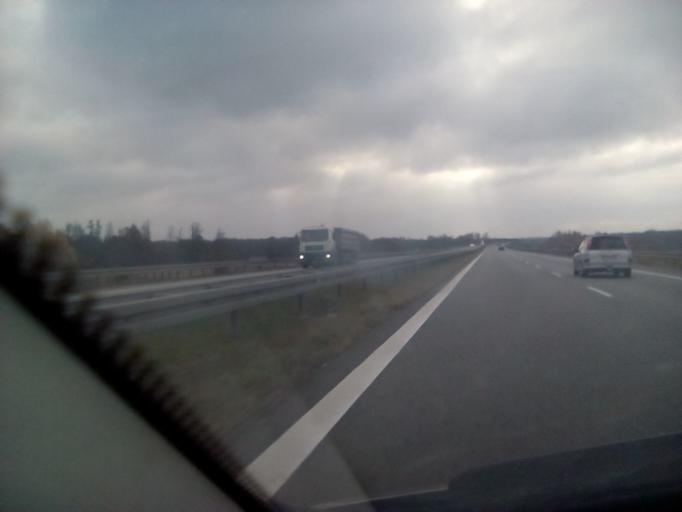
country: PL
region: Masovian Voivodeship
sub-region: Powiat bialobrzeski
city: Bialobrzegi
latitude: 51.6617
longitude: 20.9600
